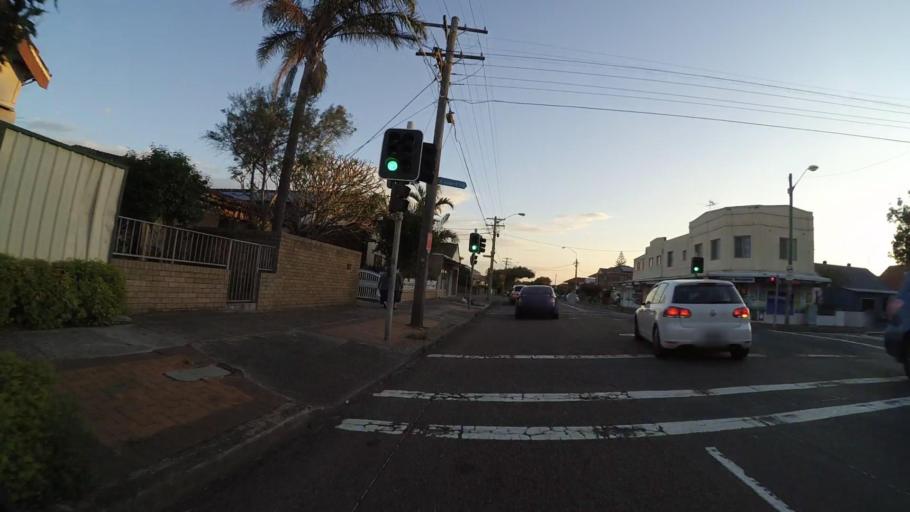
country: AU
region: New South Wales
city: Alexandria
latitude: -33.9269
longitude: 151.2062
